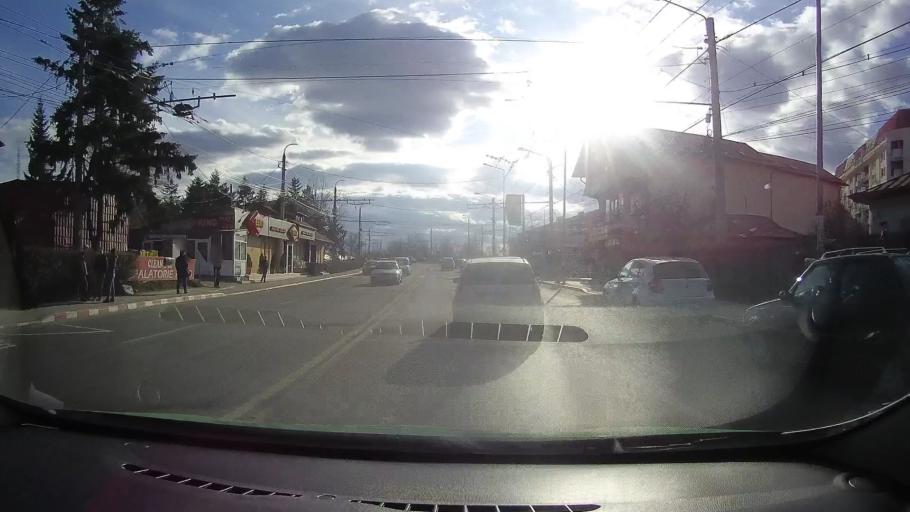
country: RO
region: Dambovita
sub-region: Comuna Lucieni
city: Lucieni
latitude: 44.8559
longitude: 25.4208
